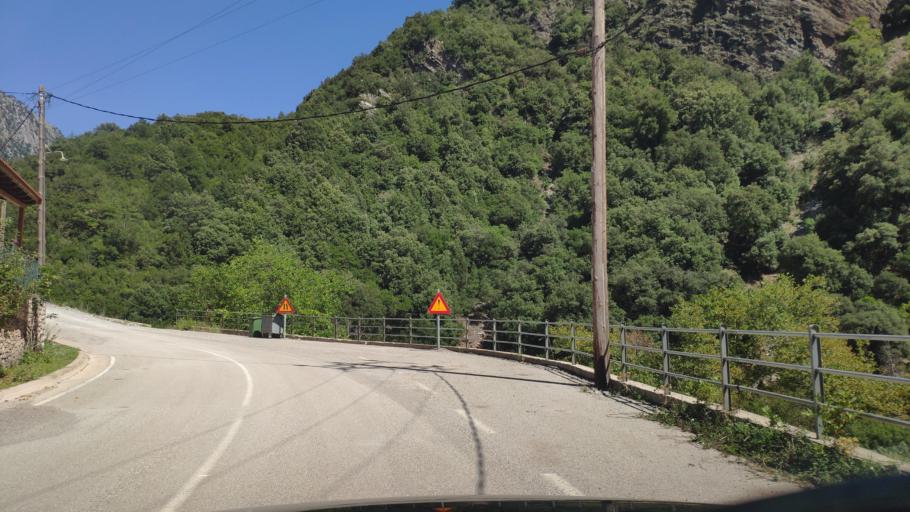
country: GR
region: Central Greece
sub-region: Nomos Evrytanias
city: Kerasochori
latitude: 39.0749
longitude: 21.6005
